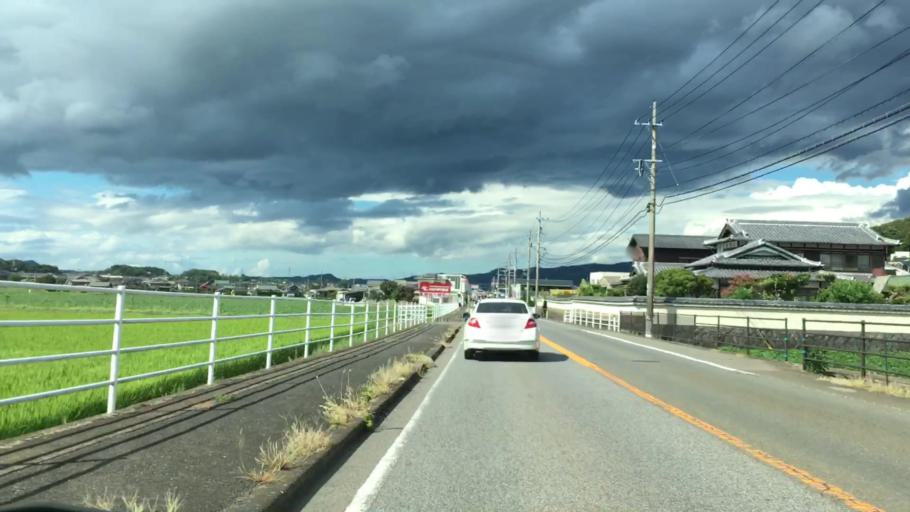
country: JP
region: Saga Prefecture
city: Imaricho-ko
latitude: 33.2468
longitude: 129.8518
